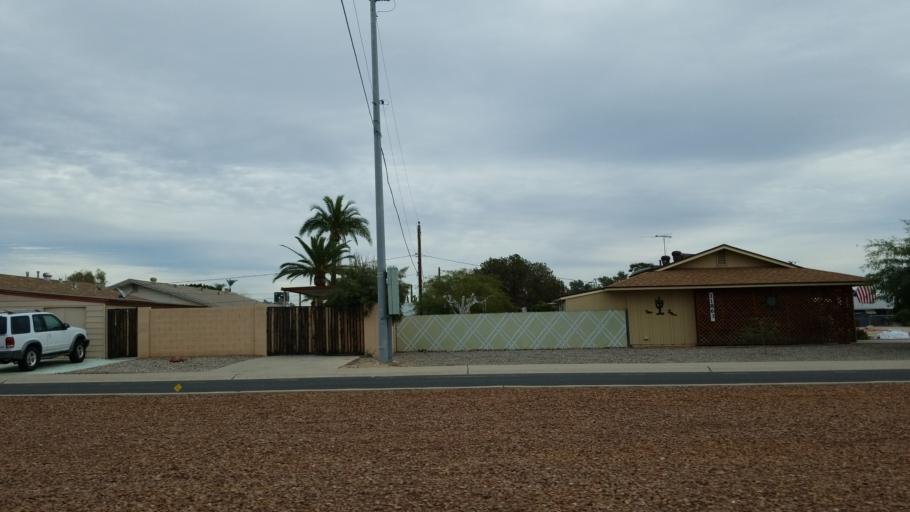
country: US
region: Arizona
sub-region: Maricopa County
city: Youngtown
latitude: 33.5934
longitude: -112.2987
